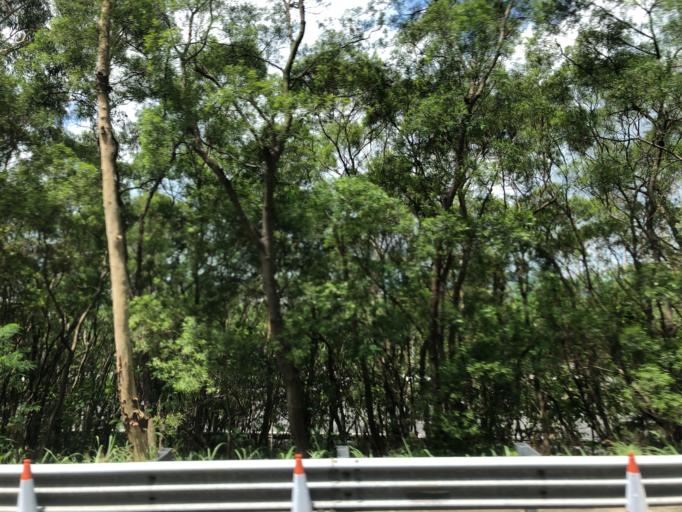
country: HK
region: Tsuen Wan
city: Tsuen Wan
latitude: 22.3564
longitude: 114.0843
